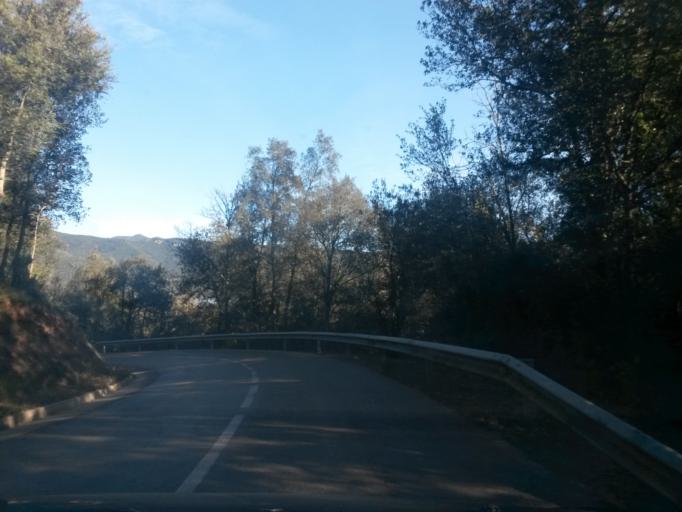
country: ES
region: Catalonia
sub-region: Provincia de Girona
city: la Cellera de Ter
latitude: 42.0201
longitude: 2.6696
